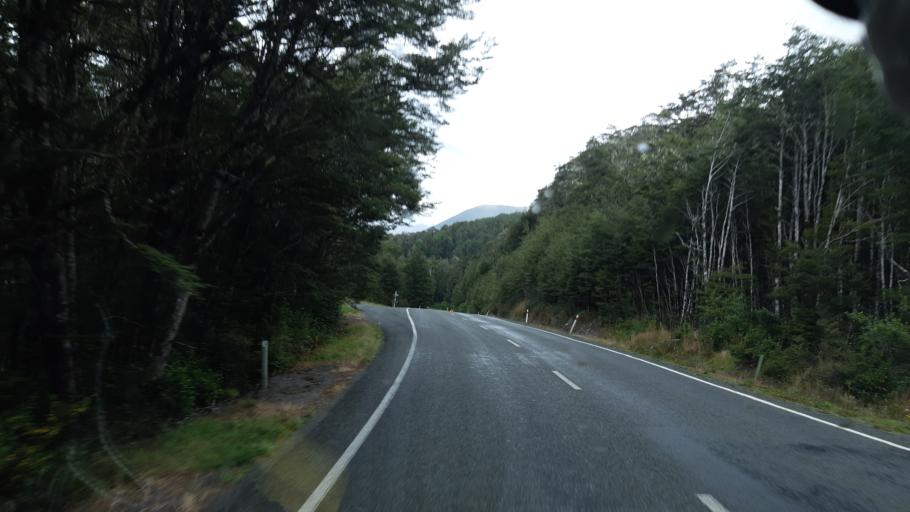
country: NZ
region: Canterbury
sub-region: Hurunui District
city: Amberley
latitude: -42.4487
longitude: 172.4041
